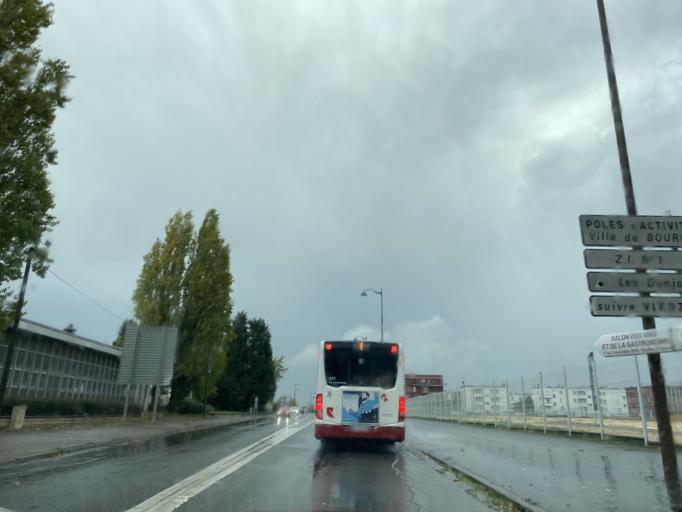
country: FR
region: Centre
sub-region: Departement du Cher
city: Bourges
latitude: 47.0673
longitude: 2.3727
